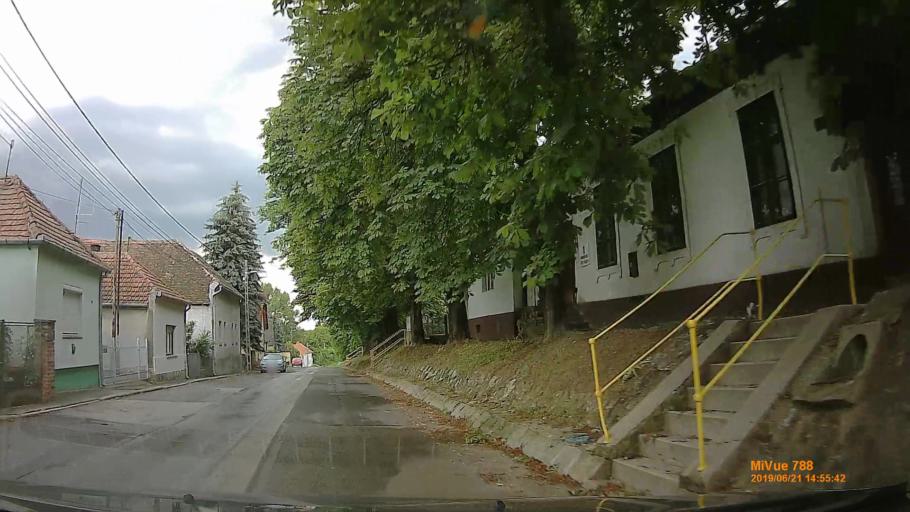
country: HU
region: Baranya
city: Hosszuheteny
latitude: 46.1213
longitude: 18.3107
